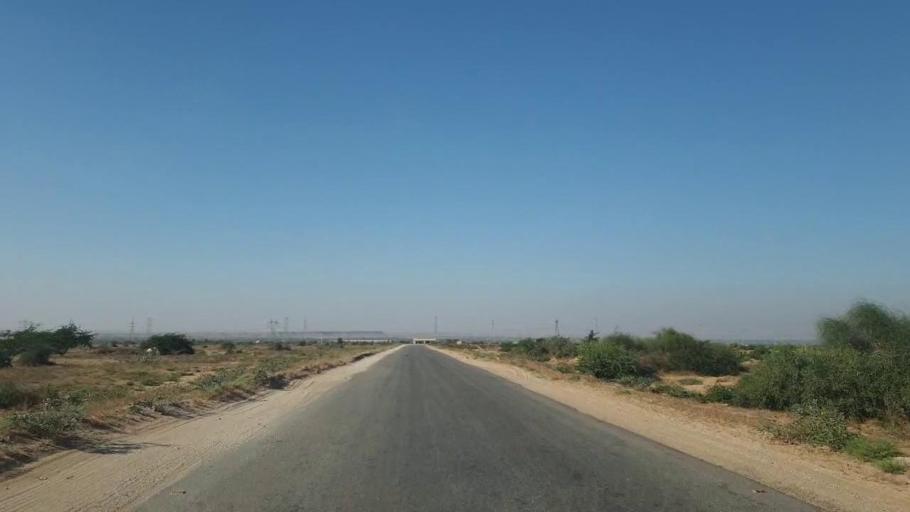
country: PK
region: Sindh
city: Gharo
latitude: 25.1675
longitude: 67.6613
